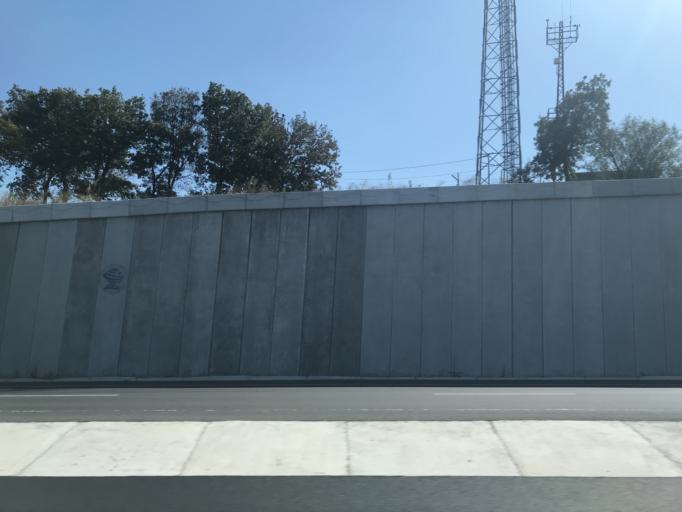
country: TR
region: Tekirdag
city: Muratli
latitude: 41.1562
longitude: 27.5081
